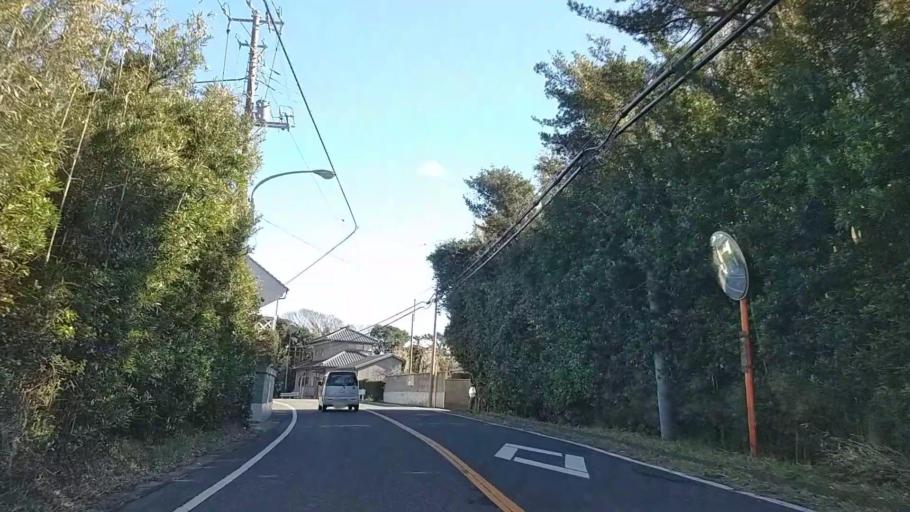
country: JP
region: Chiba
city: Tateyama
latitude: 34.9090
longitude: 139.8544
